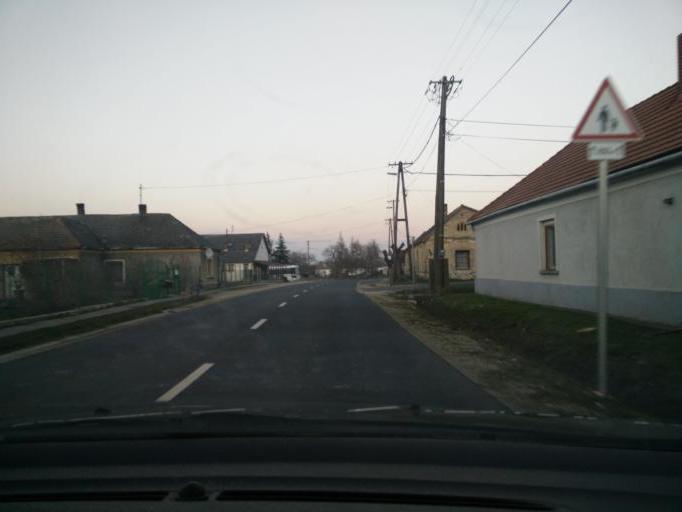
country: HU
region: Veszprem
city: Csabrendek
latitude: 47.0438
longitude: 17.3243
